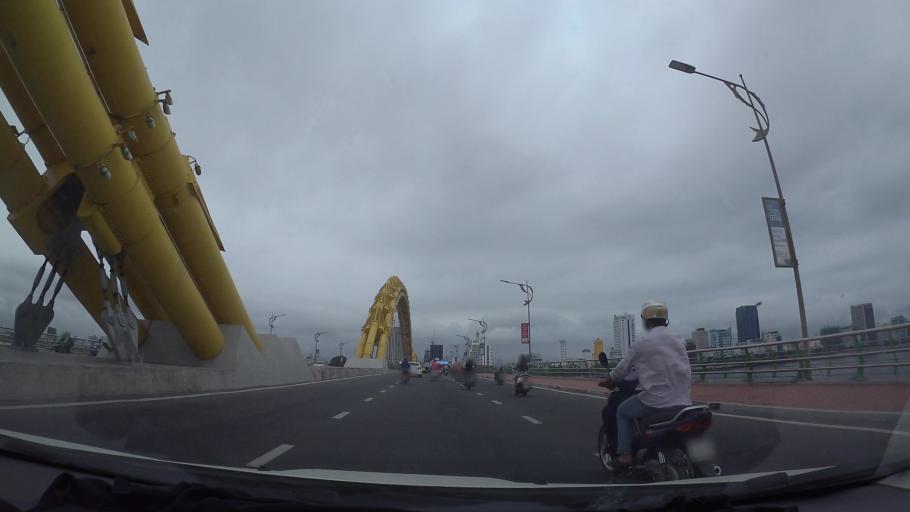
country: VN
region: Da Nang
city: Son Tra
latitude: 16.0612
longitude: 108.2284
